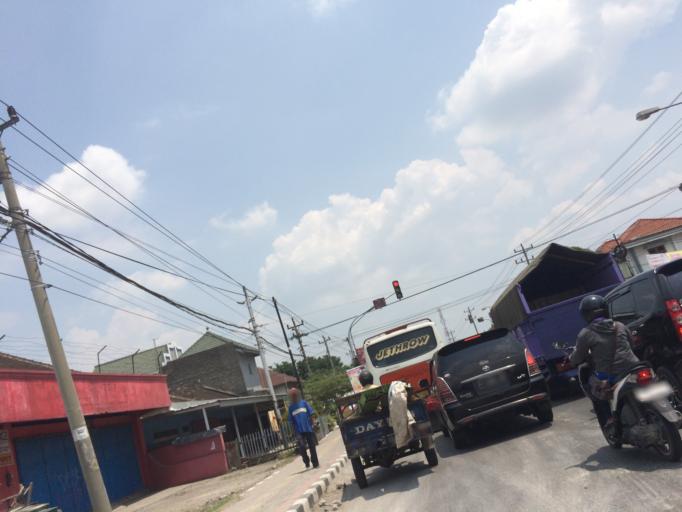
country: ID
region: Central Java
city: Grogol
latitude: -7.6215
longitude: 110.8216
